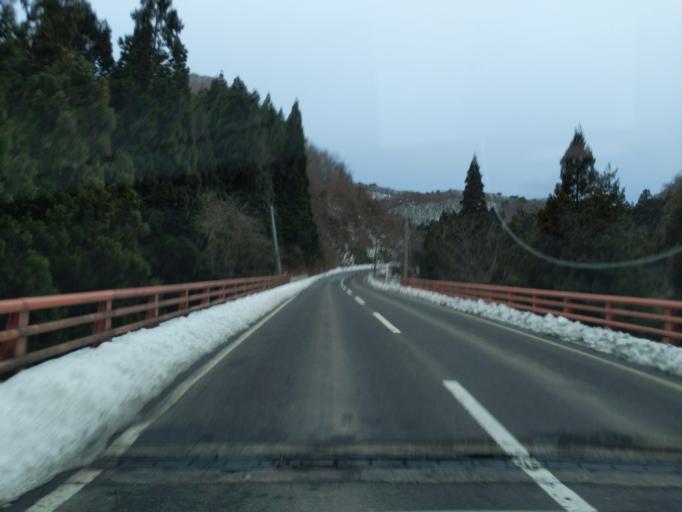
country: JP
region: Iwate
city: Mizusawa
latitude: 39.1037
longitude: 141.2697
